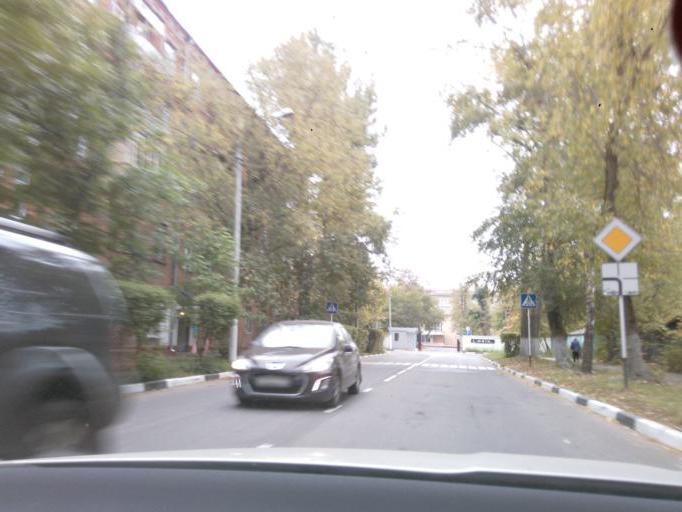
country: RU
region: Moskovskaya
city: Dolgoprudnyy
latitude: 55.9312
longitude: 37.5166
